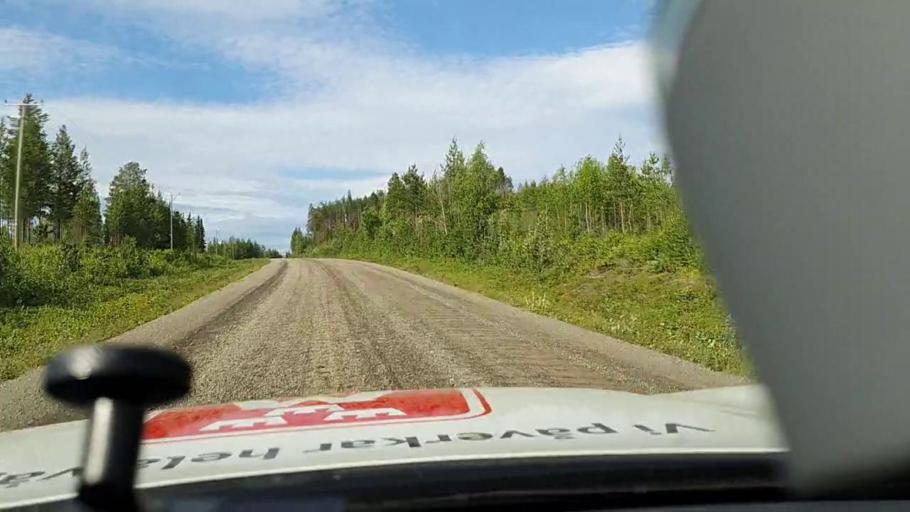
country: SE
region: Norrbotten
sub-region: Alvsbyns Kommun
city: AElvsbyn
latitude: 66.1665
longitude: 21.0574
